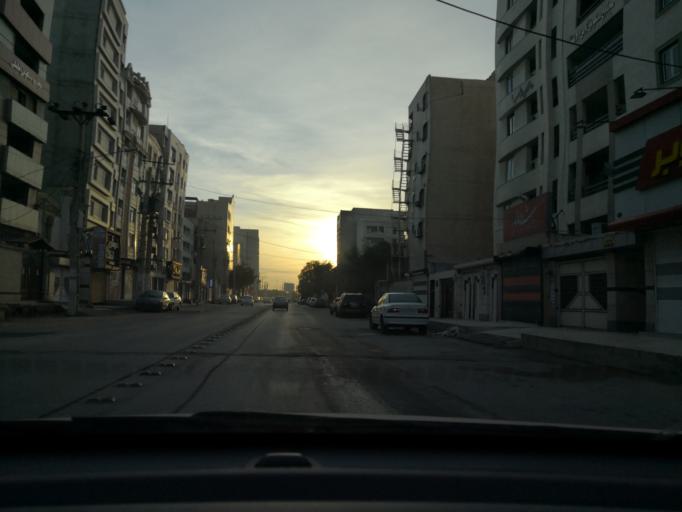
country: IR
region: Khuzestan
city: Ahvaz
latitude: 31.3490
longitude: 48.6914
